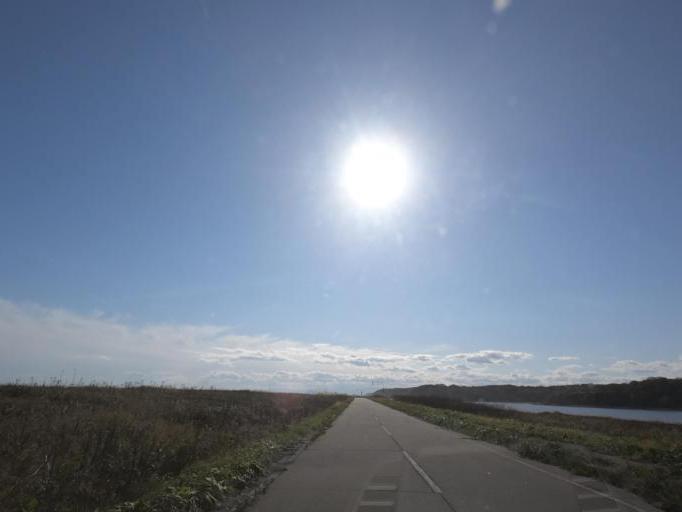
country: JP
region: Hokkaido
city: Obihiro
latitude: 42.5828
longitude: 143.5321
